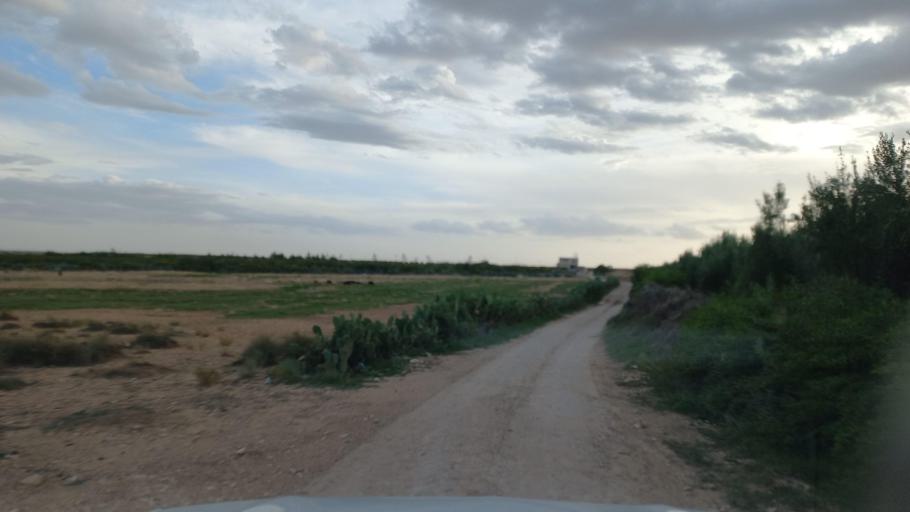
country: TN
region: Al Qasrayn
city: Sbiba
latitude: 35.4281
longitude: 9.0981
